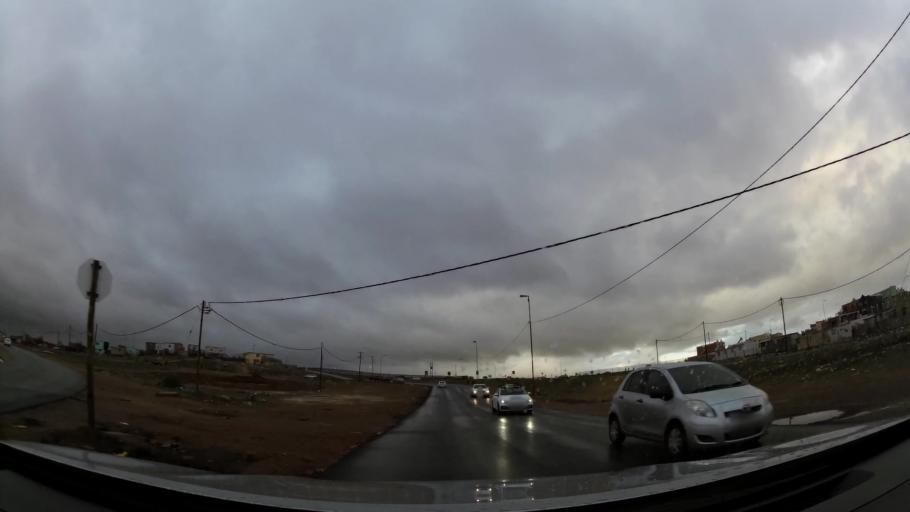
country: ZA
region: Eastern Cape
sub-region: Nelson Mandela Bay Metropolitan Municipality
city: Port Elizabeth
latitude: -33.8870
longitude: 25.5586
